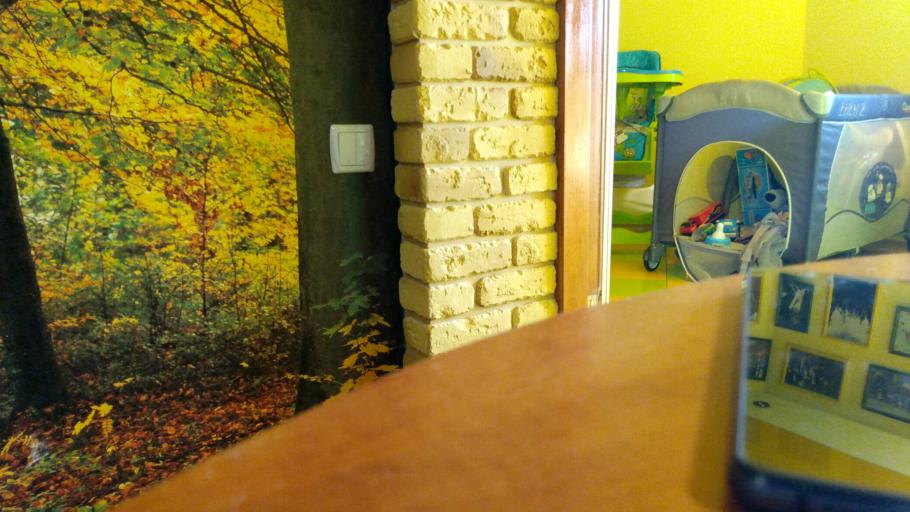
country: RU
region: Tverskaya
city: Kalashnikovo
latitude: 57.2984
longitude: 35.3411
